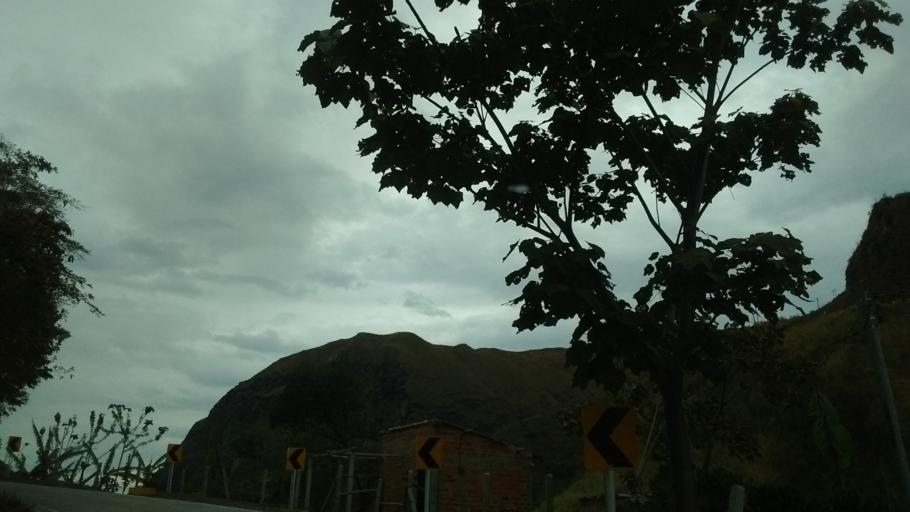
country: CO
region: Cauca
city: La Sierra
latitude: 2.1521
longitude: -76.7679
